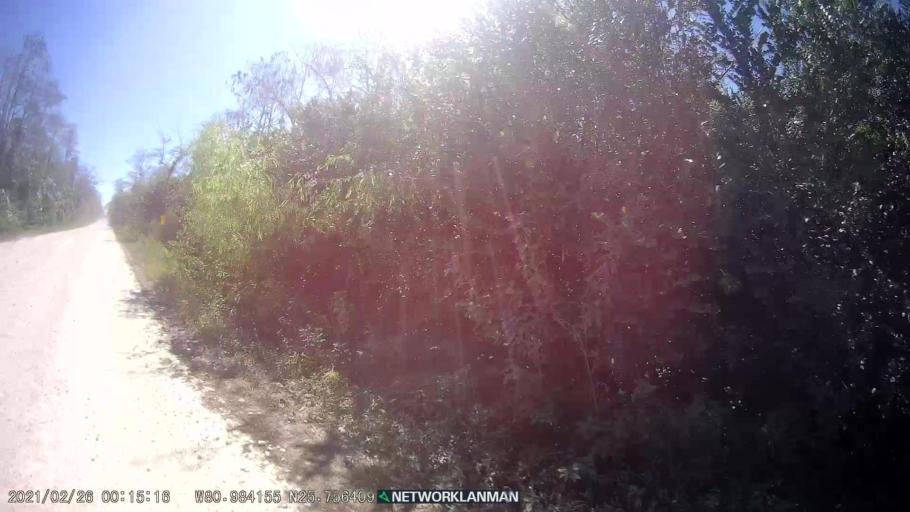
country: US
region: Florida
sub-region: Miami-Dade County
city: The Hammocks
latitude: 25.7562
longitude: -80.9835
